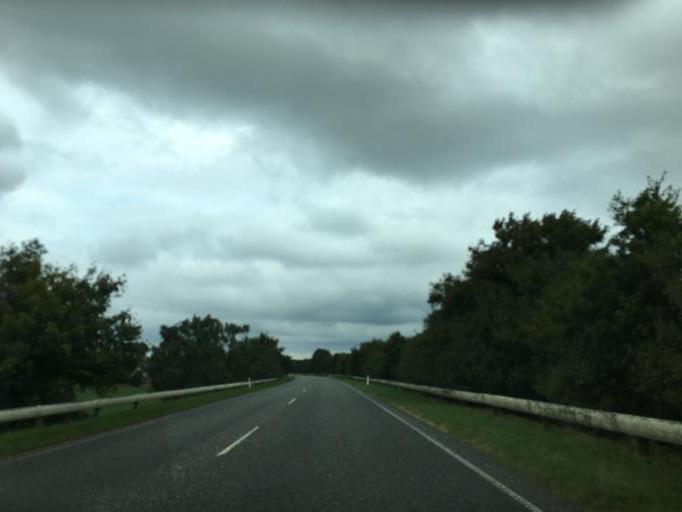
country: DK
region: South Denmark
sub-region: Kolding Kommune
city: Kolding
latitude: 55.5782
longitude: 9.4997
